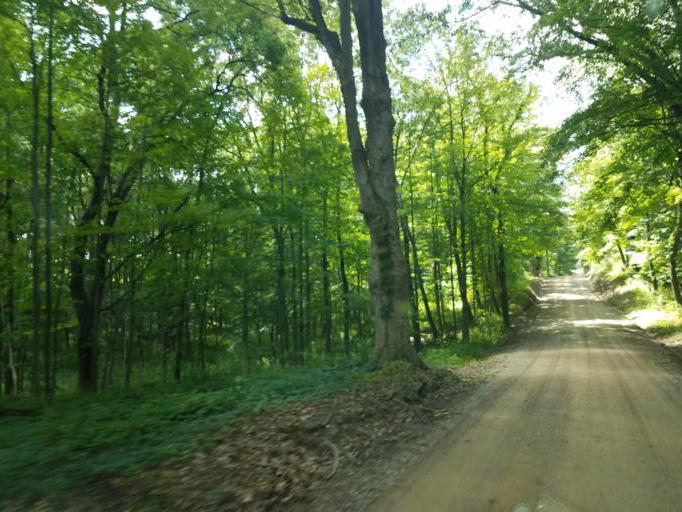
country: US
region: Ohio
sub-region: Knox County
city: Danville
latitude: 40.4217
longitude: -82.2917
